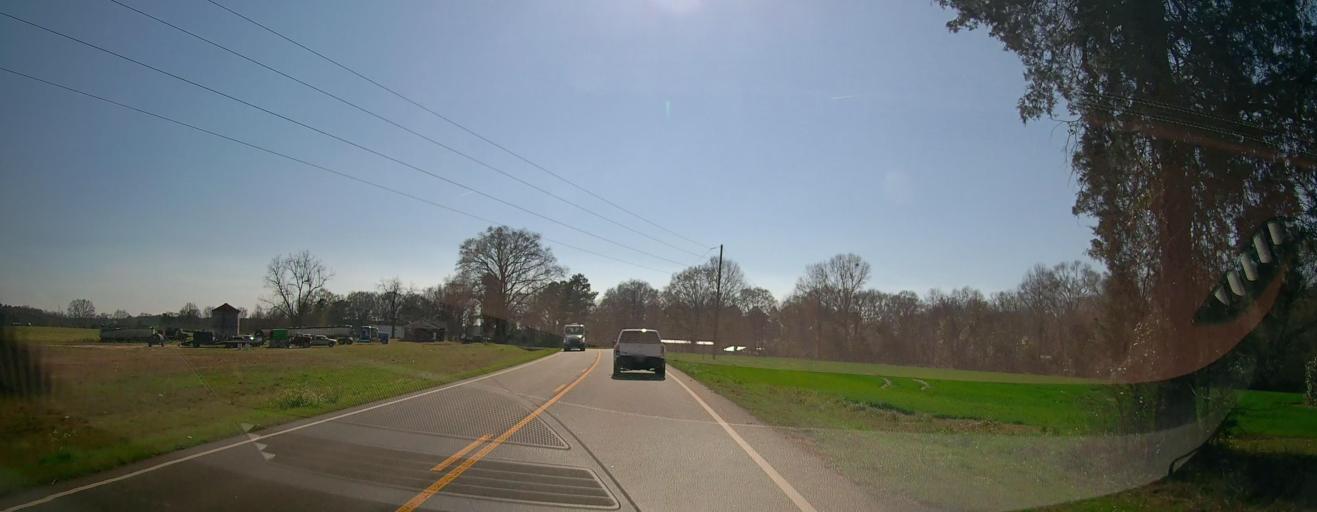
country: US
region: Georgia
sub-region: Macon County
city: Montezuma
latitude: 32.3092
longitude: -83.9040
